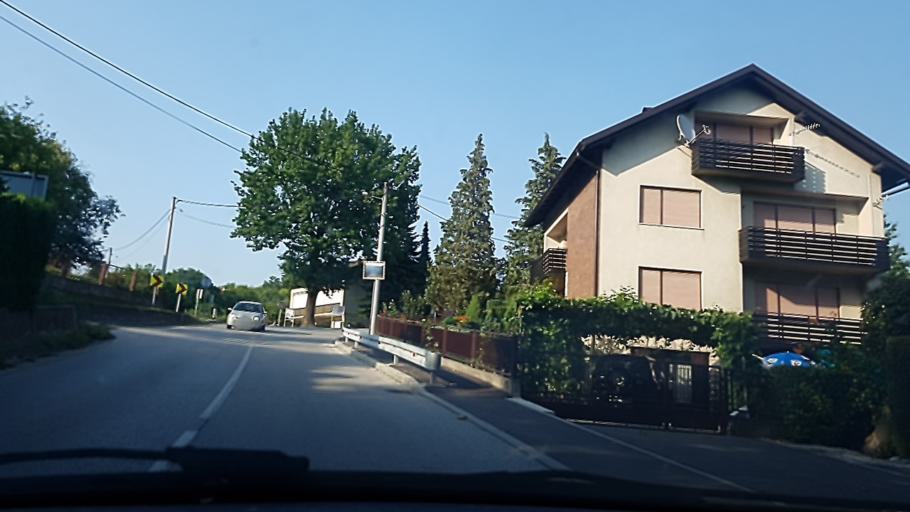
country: HR
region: Zagrebacka
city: Pojatno
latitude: 45.9236
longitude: 15.8091
